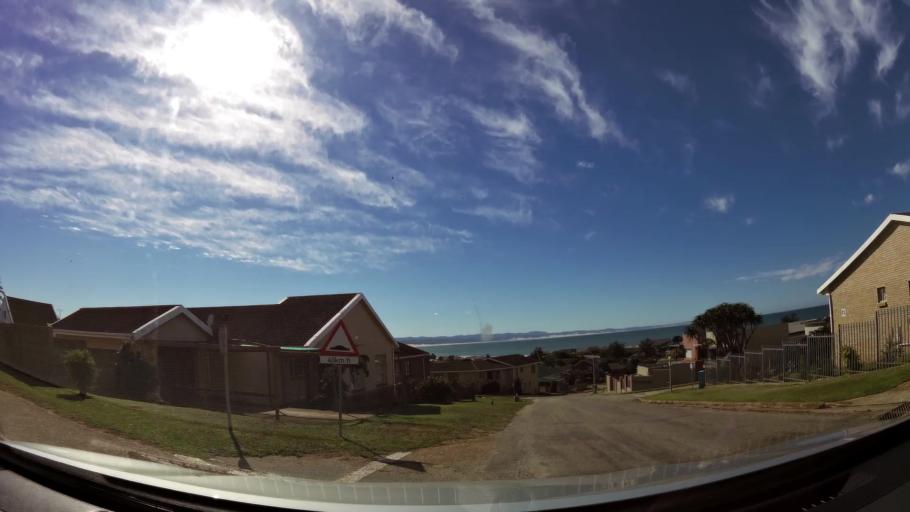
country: ZA
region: Eastern Cape
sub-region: Cacadu District Municipality
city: Jeffrey's Bay
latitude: -34.0188
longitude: 24.9237
